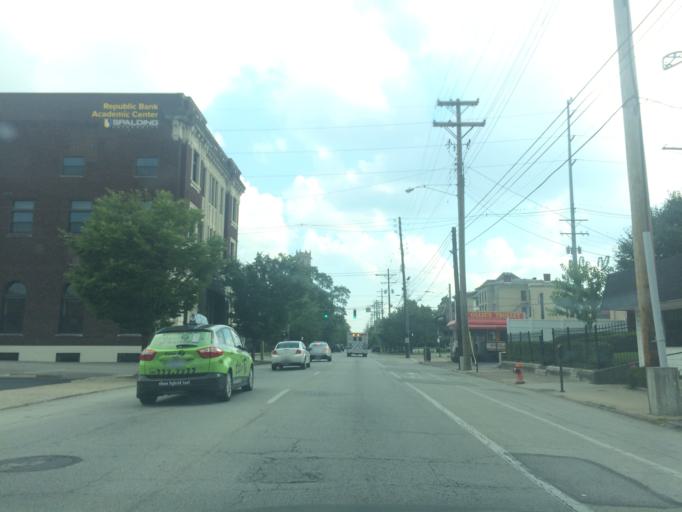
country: US
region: Kentucky
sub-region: Jefferson County
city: Louisville
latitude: 38.2394
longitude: -85.7579
